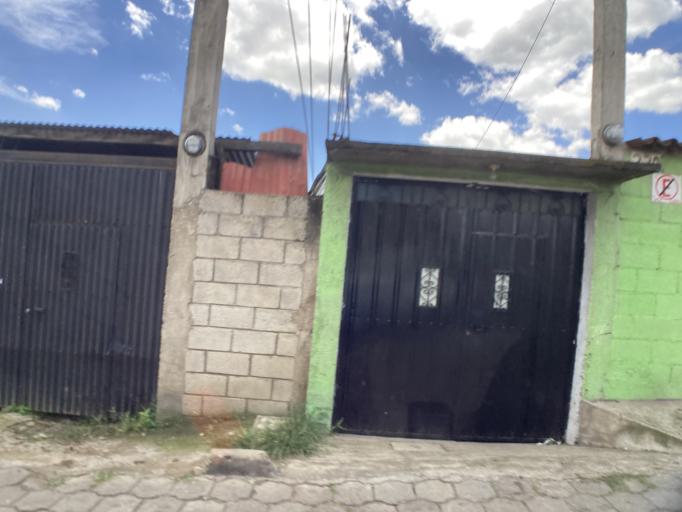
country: GT
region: Sacatepequez
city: Ciudad Vieja
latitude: 14.5249
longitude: -90.7535
